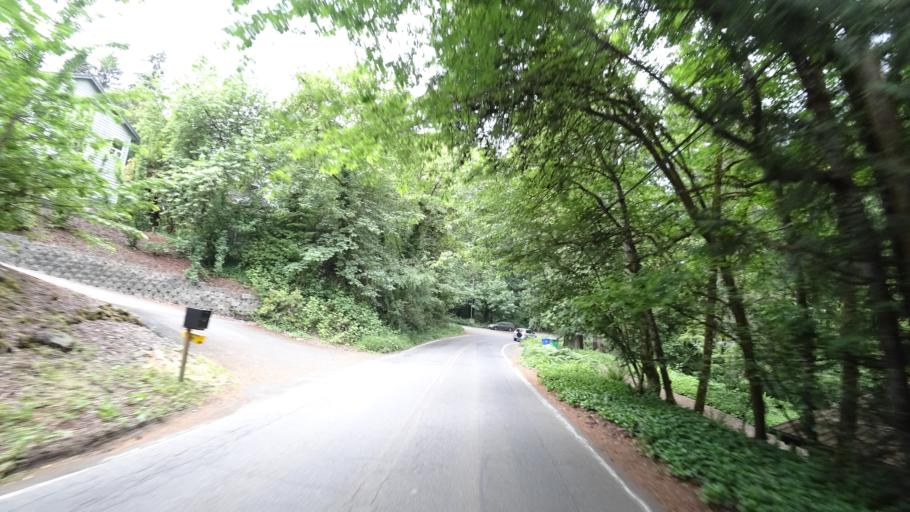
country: US
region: Oregon
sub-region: Clackamas County
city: Lake Oswego
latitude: 45.4554
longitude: -122.7015
